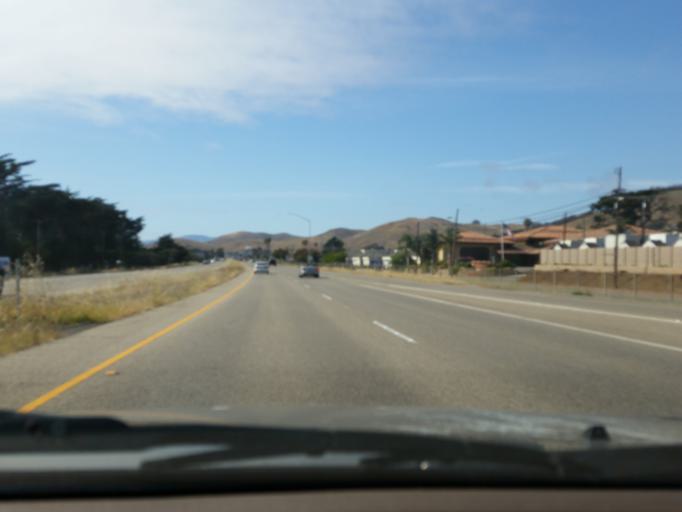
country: US
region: California
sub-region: San Luis Obispo County
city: Morro Bay
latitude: 35.3817
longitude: -120.8560
